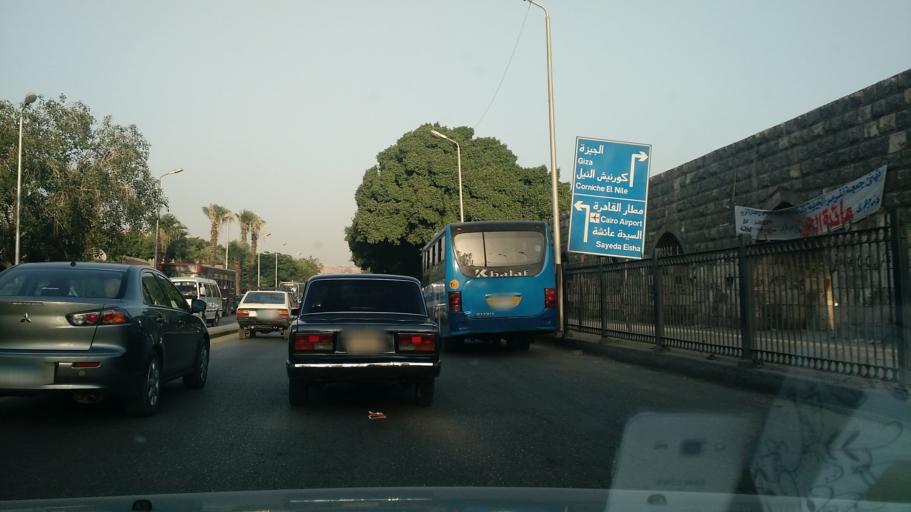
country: EG
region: Al Jizah
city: Al Jizah
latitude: 30.0192
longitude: 31.2485
